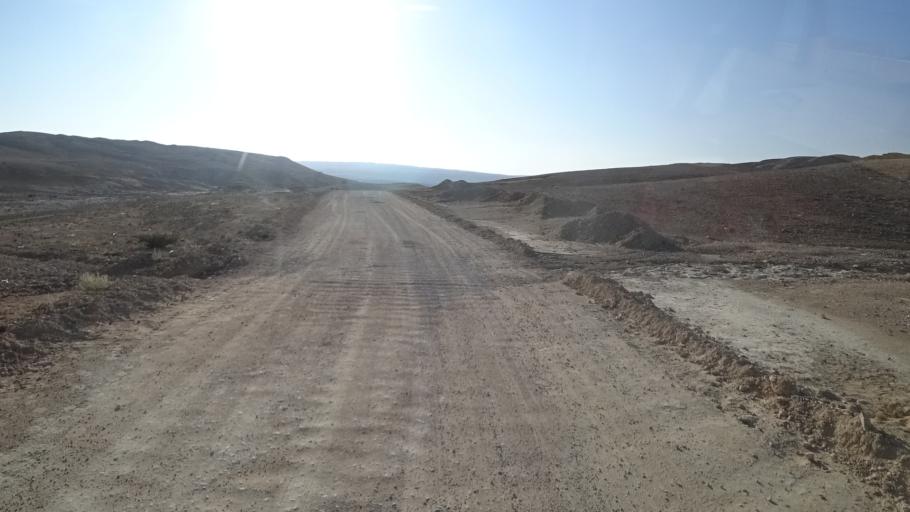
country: OM
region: Zufar
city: Salalah
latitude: 17.2424
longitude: 53.9131
